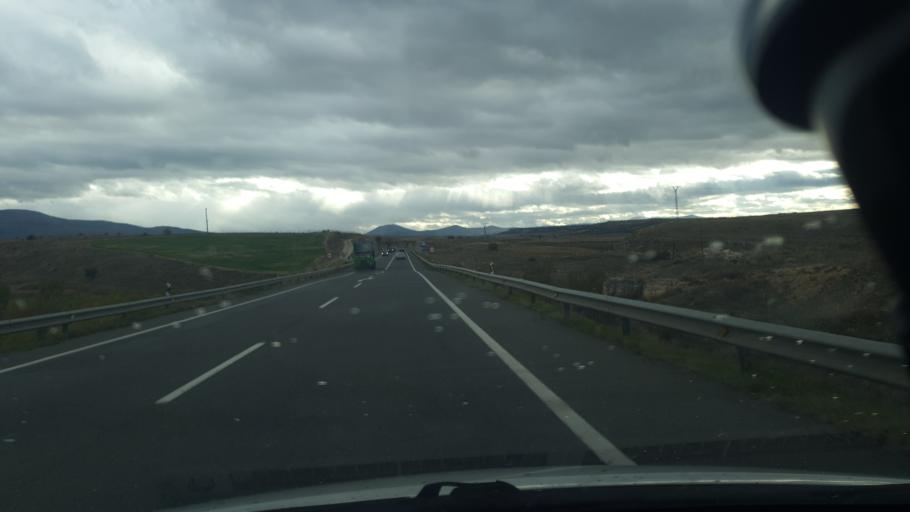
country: ES
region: Castille and Leon
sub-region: Provincia de Segovia
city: Segovia
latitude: 40.9055
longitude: -4.1629
